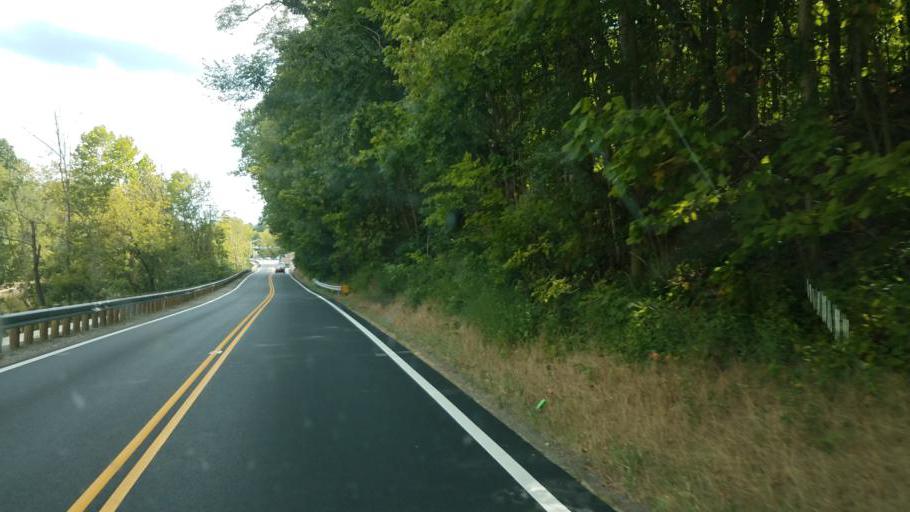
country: US
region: Ohio
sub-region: Delaware County
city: Powell
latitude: 40.1602
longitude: -83.0457
